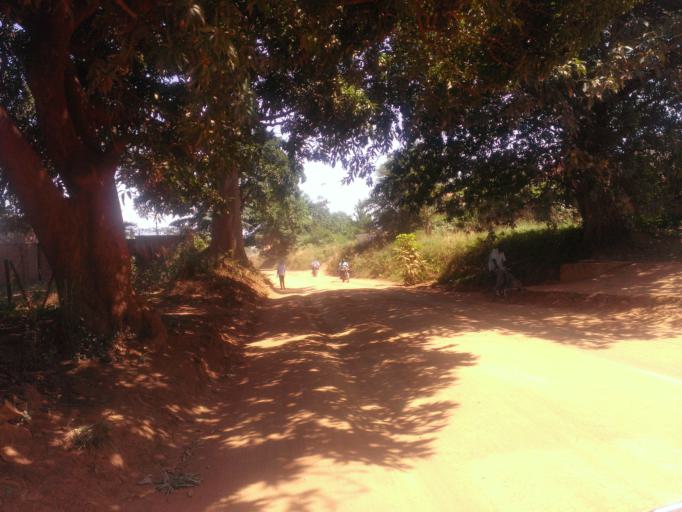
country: UG
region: Northern Region
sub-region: Gulu District
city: Gulu
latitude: 2.7810
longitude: 32.2948
